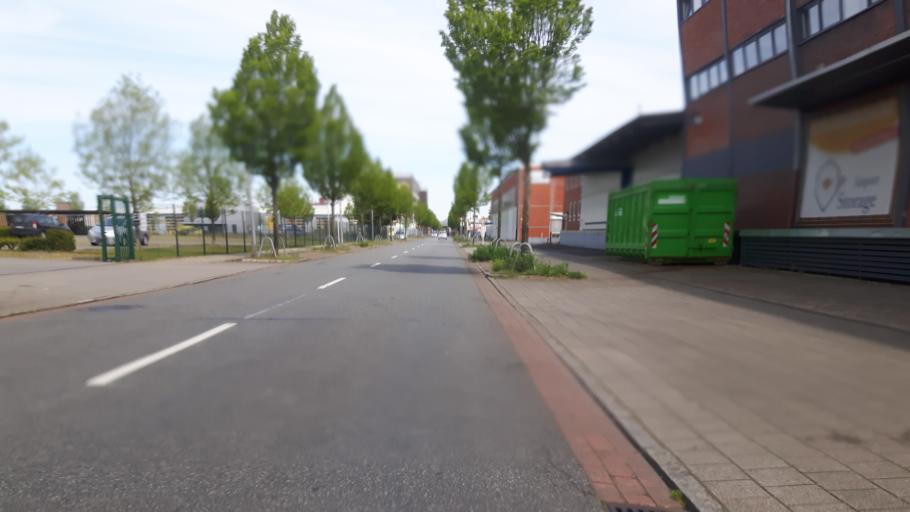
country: DE
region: Bremen
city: Bremen
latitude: 53.0577
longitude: 8.7770
